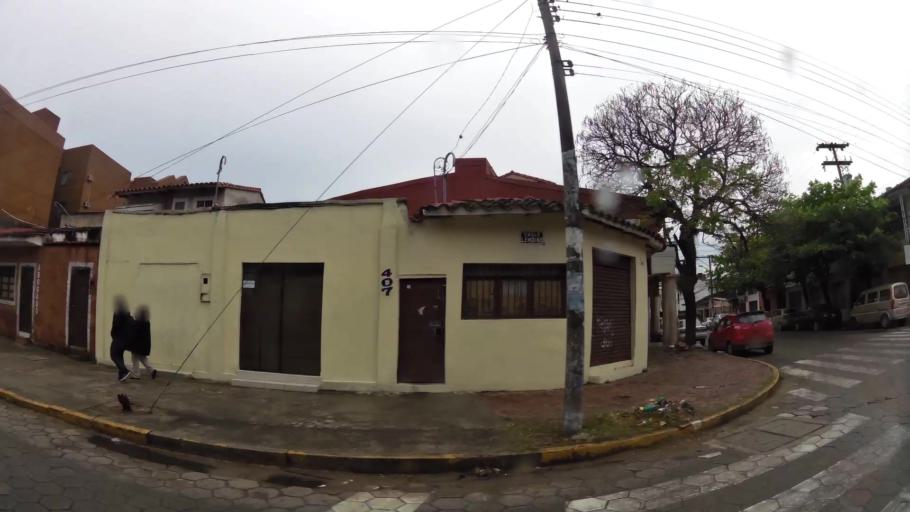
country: BO
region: Santa Cruz
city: Santa Cruz de la Sierra
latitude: -17.7908
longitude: -63.1848
